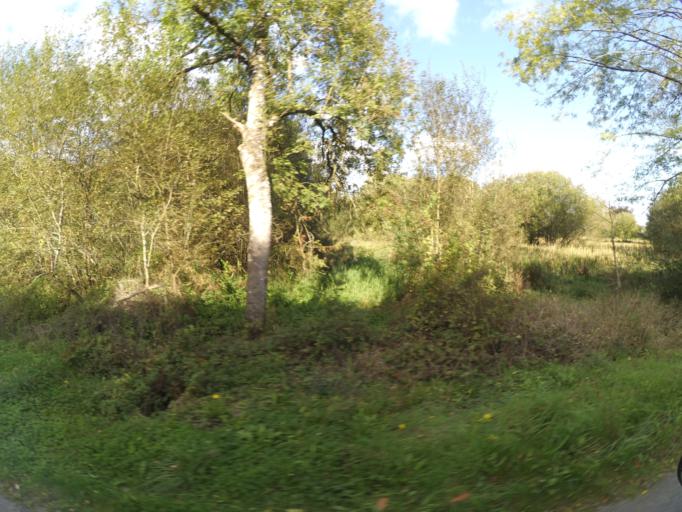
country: FR
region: Brittany
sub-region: Departement du Morbihan
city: Peillac
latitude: 47.7255
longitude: -2.2159
